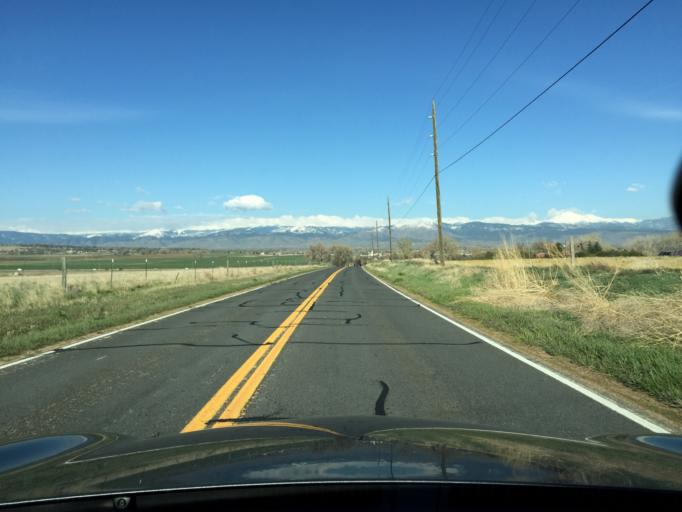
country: US
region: Colorado
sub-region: Boulder County
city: Longmont
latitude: 40.1163
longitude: -105.0933
